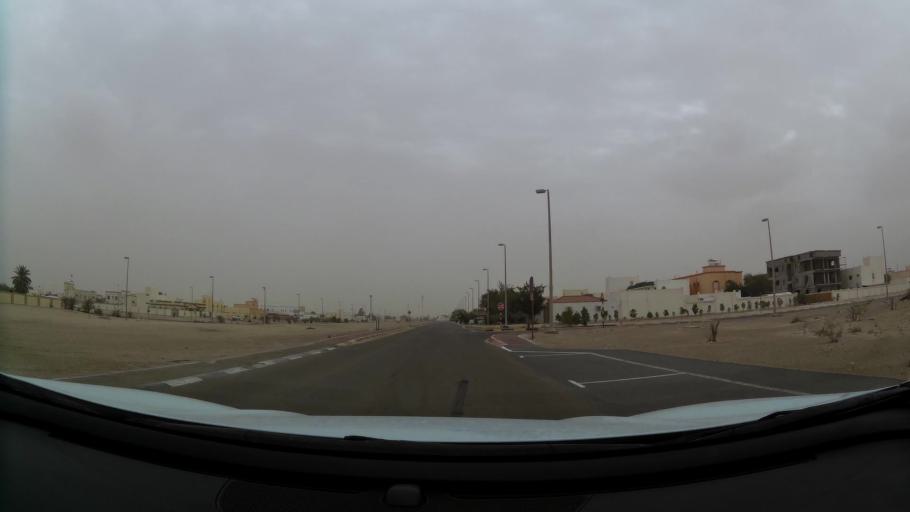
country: AE
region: Abu Dhabi
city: Abu Dhabi
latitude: 24.4244
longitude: 54.7368
